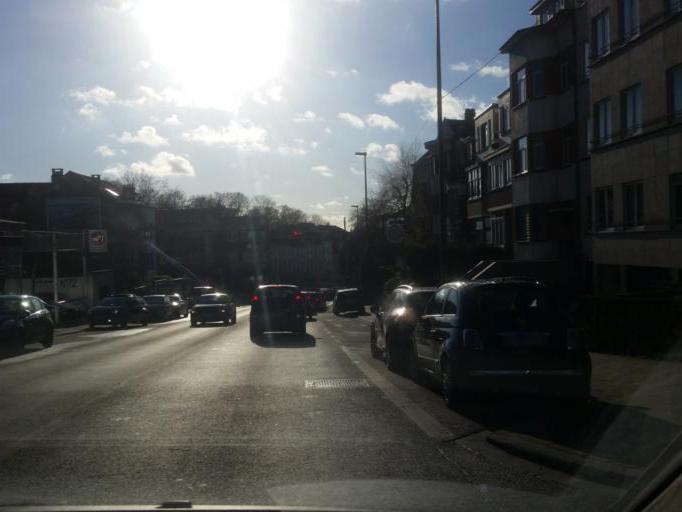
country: BE
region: Flanders
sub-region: Provincie Vlaams-Brabant
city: Linkebeek
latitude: 50.7988
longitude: 4.3756
